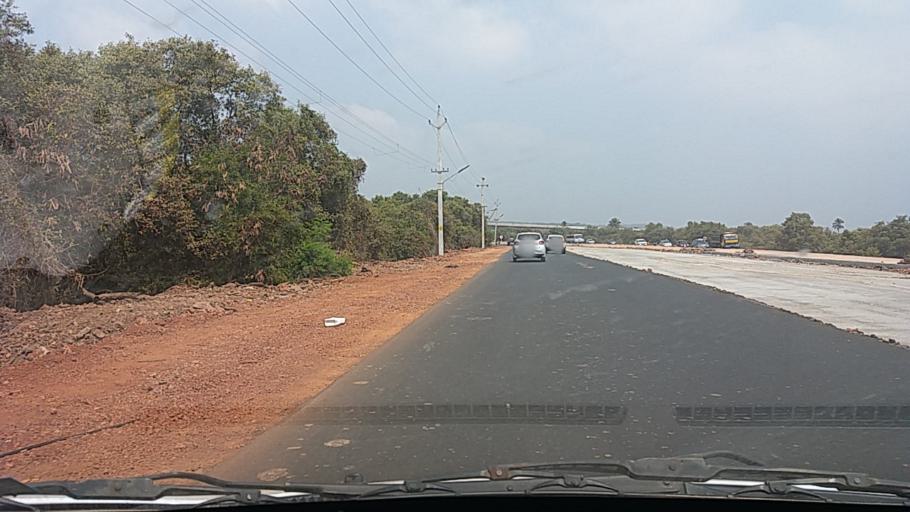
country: IN
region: Goa
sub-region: North Goa
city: Panaji
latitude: 15.4876
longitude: 73.8458
